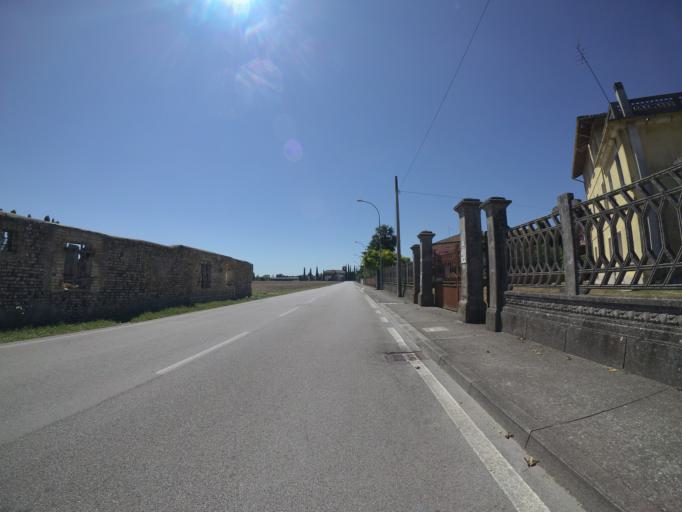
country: IT
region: Friuli Venezia Giulia
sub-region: Provincia di Udine
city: Rivignano
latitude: 45.8708
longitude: 13.0382
